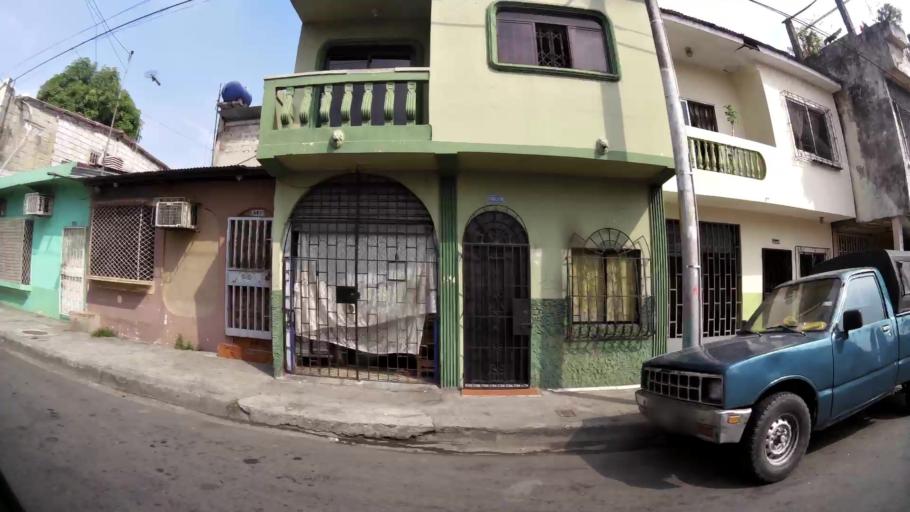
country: EC
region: Guayas
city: Guayaquil
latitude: -2.2191
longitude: -79.9062
